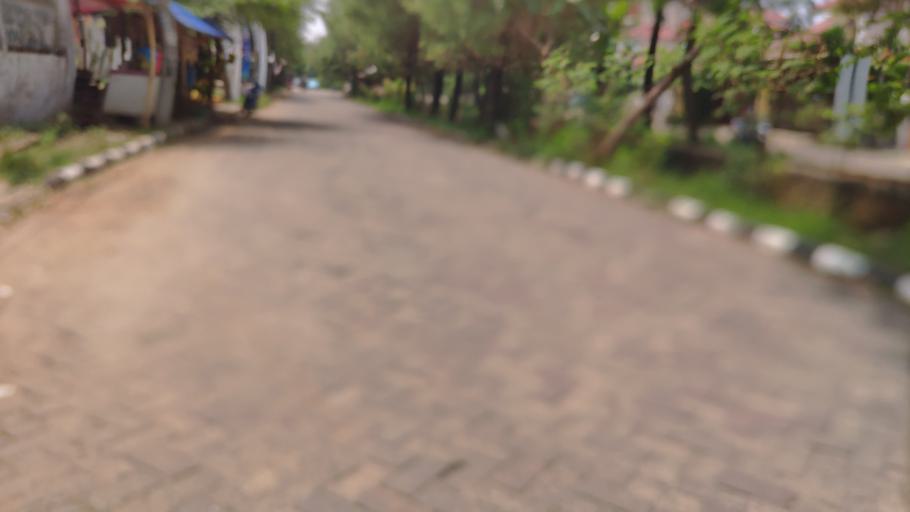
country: ID
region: West Java
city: Sawangan
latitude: -6.4005
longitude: 106.7930
